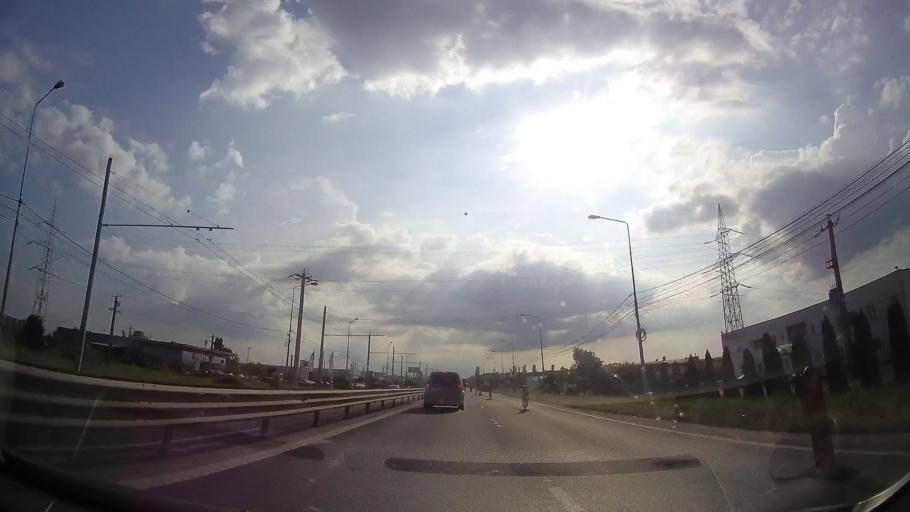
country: RO
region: Timis
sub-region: Comuna Ghiroda
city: Ghiroda
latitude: 45.7741
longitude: 21.2934
